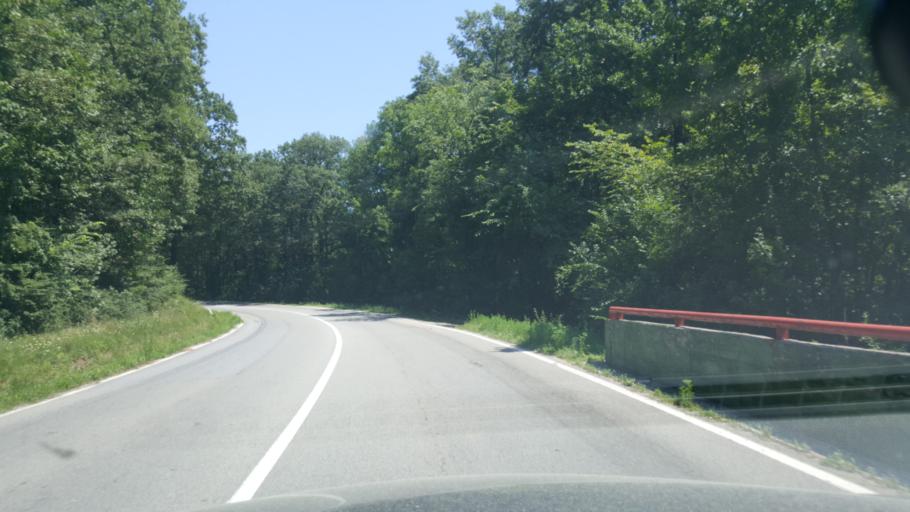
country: RS
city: Rusanj
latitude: 44.6839
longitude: 20.5128
